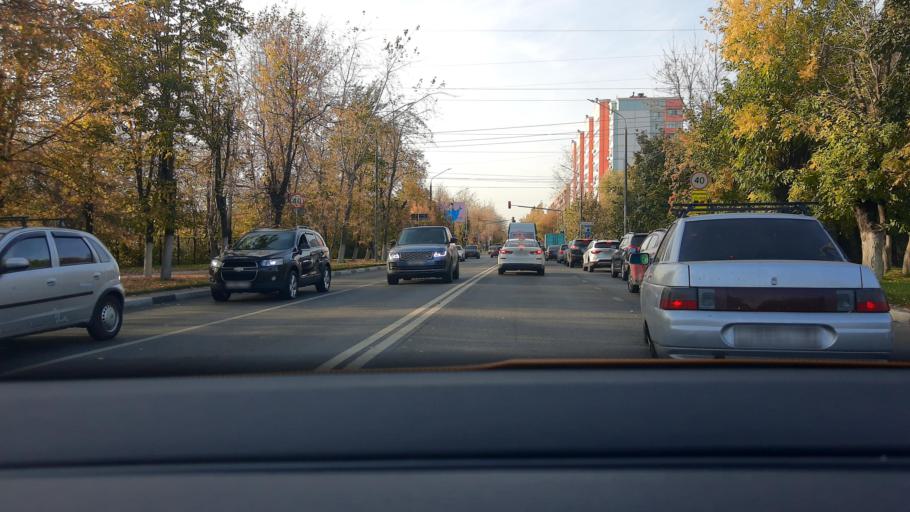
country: RU
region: Moskovskaya
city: Reutov
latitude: 55.7653
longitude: 37.8515
